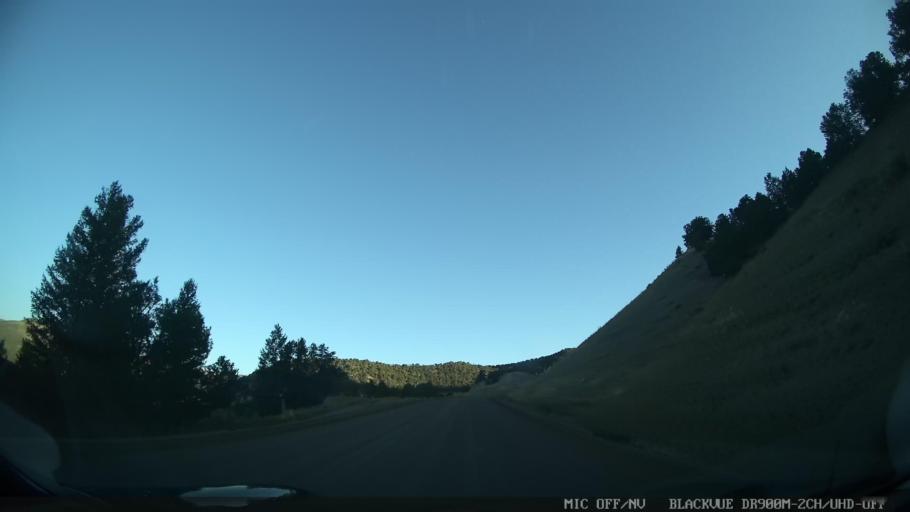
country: US
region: Colorado
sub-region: Grand County
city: Kremmling
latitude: 39.9445
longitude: -106.5289
